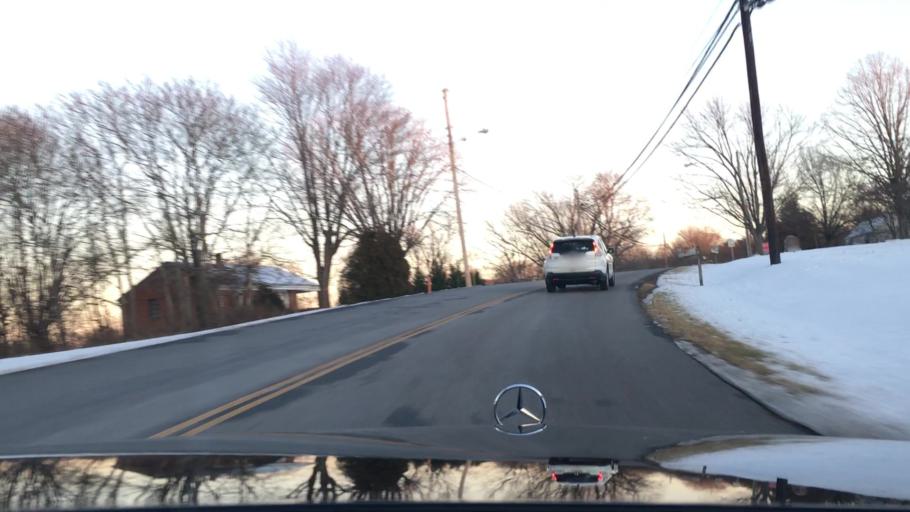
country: US
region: Virginia
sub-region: City of Lynchburg
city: West Lynchburg
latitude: 37.3616
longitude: -79.1942
